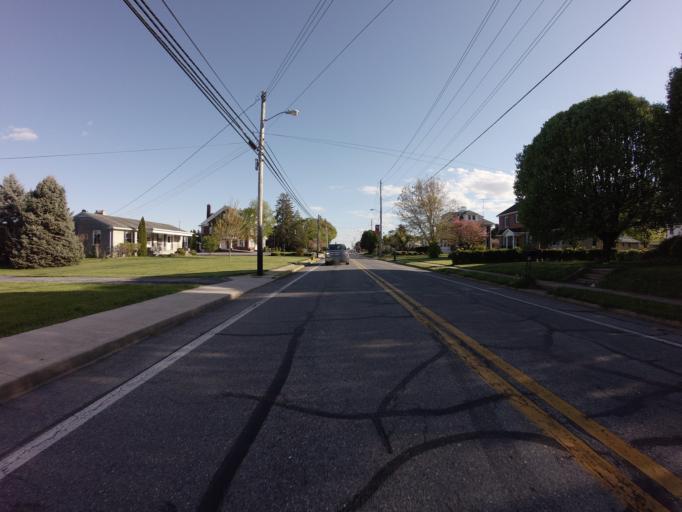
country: US
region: Maryland
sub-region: Frederick County
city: Woodsboro
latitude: 39.5306
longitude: -77.3149
